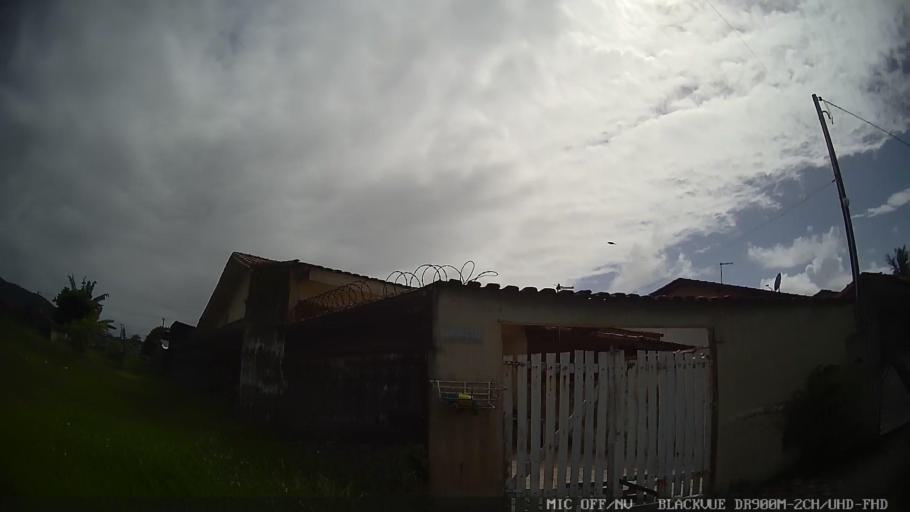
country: BR
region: Sao Paulo
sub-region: Itanhaem
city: Itanhaem
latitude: -24.1410
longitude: -46.7114
